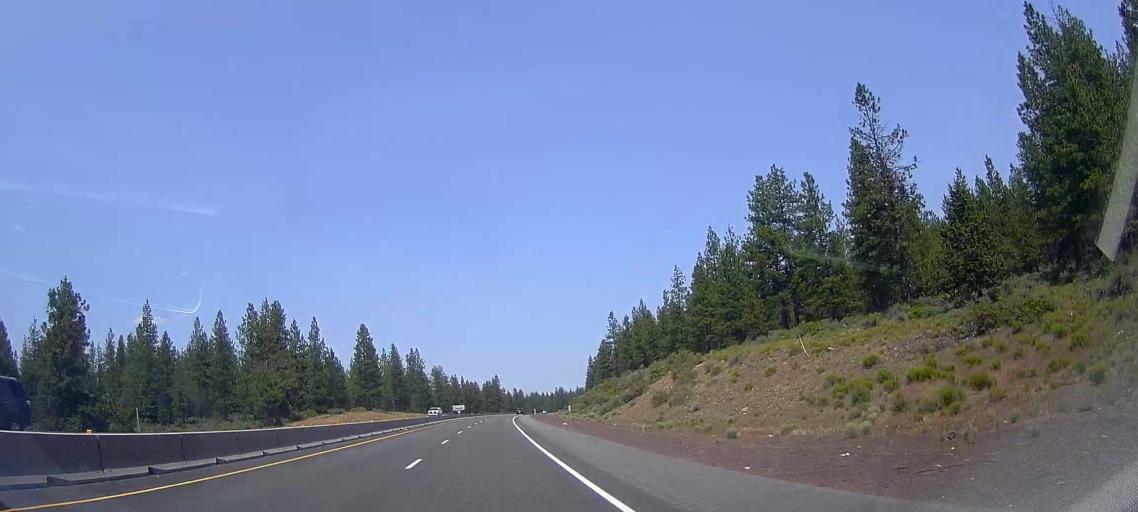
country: US
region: Oregon
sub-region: Deschutes County
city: Deschutes River Woods
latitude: 43.9769
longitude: -121.3452
